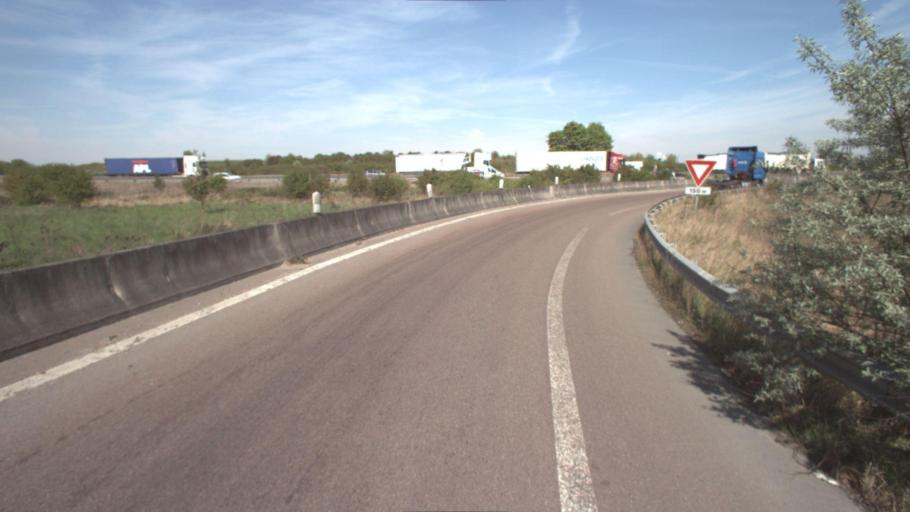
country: FR
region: Ile-de-France
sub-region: Departement de Seine-et-Marne
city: Mitry-Mory
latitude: 48.9979
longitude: 2.6346
